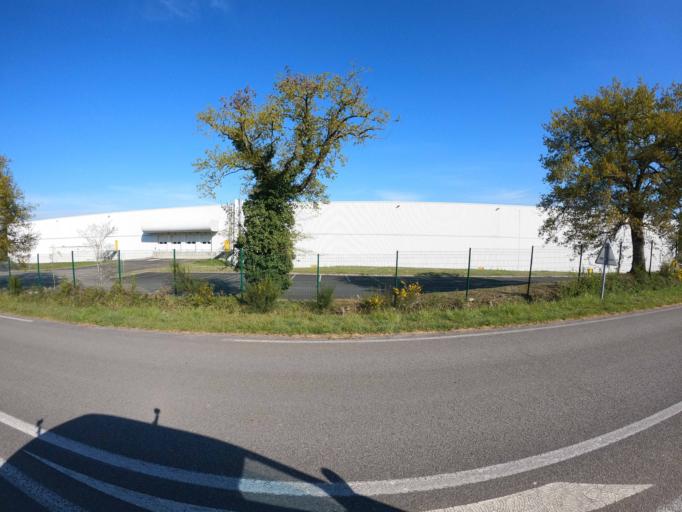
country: FR
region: Pays de la Loire
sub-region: Departement de la Vendee
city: Mortagne-sur-Sevre
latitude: 46.9788
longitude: -0.9651
